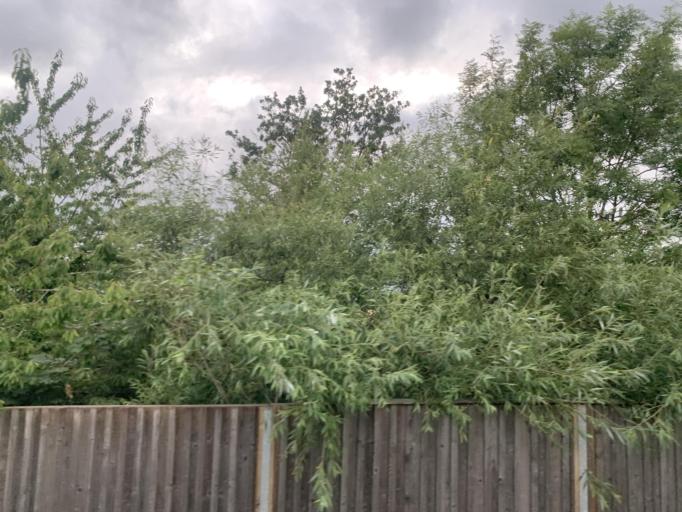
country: GB
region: England
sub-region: West Berkshire
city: Eton
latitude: 51.4965
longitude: -0.6198
